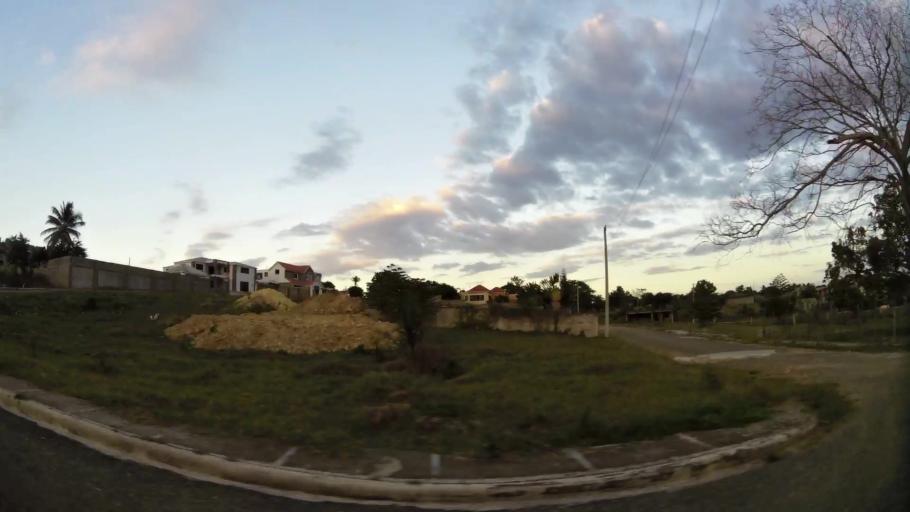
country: DO
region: Nacional
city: La Agustina
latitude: 18.5690
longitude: -69.9373
